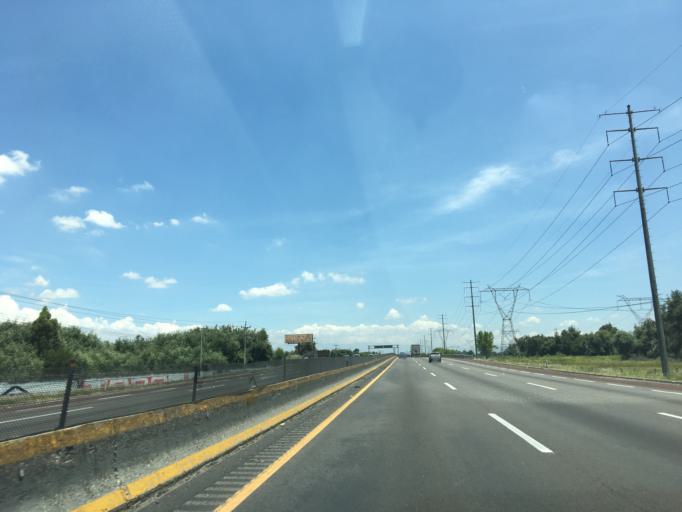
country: MX
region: Puebla
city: San Miguel Xoxtla
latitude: 19.1807
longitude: -98.3147
